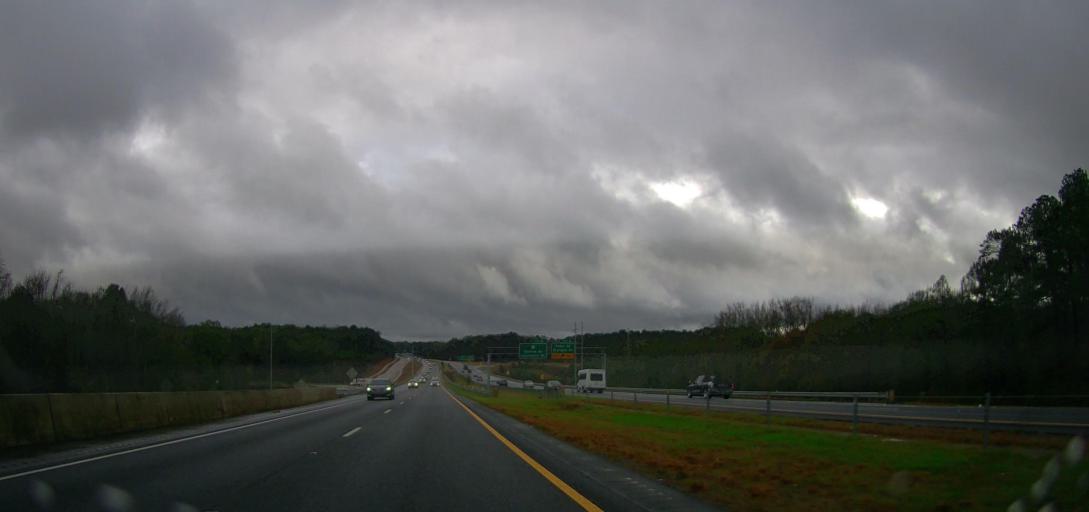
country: US
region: Georgia
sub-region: Clarke County
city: Athens
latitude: 33.9671
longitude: -83.3536
